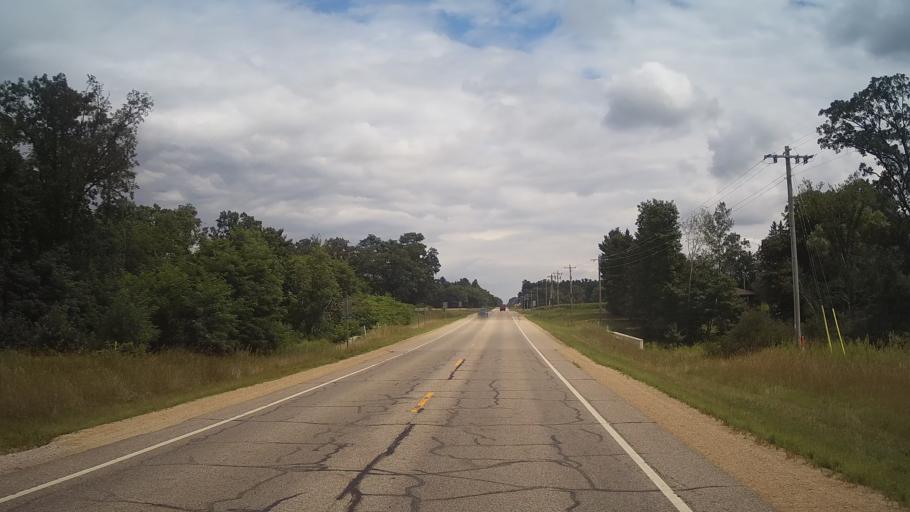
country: US
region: Wisconsin
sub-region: Waushara County
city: Wautoma
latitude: 44.0684
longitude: -89.3400
